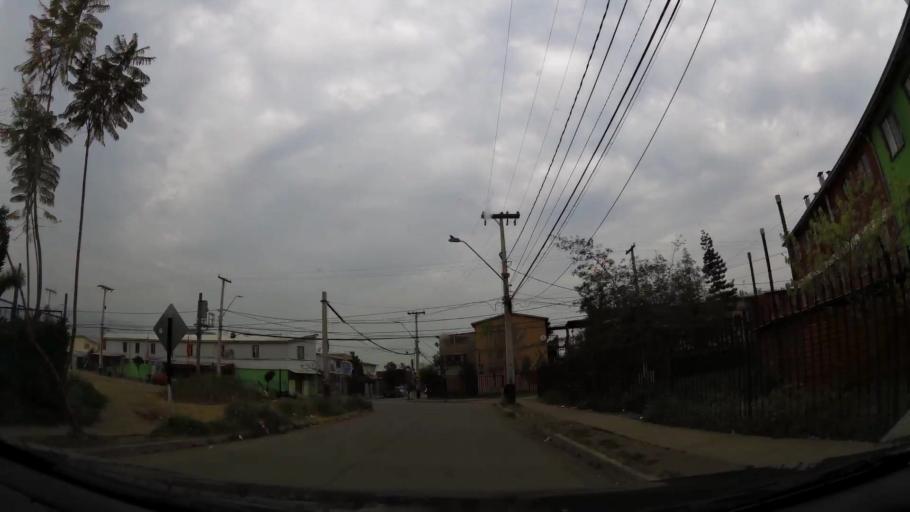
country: CL
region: Santiago Metropolitan
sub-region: Provincia de Chacabuco
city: Chicureo Abajo
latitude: -33.1882
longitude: -70.6648
